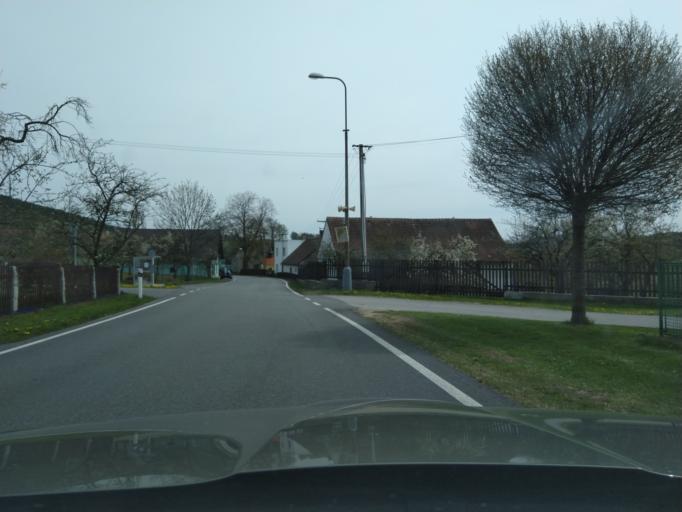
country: CZ
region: Jihocesky
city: Ckyne
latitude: 49.1161
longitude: 13.7996
